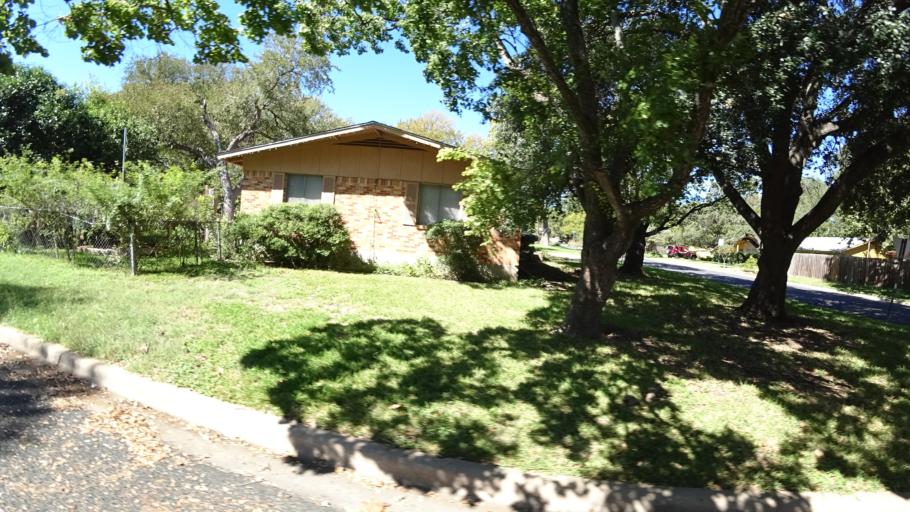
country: US
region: Texas
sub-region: Travis County
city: Rollingwood
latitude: 30.2268
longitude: -97.7989
